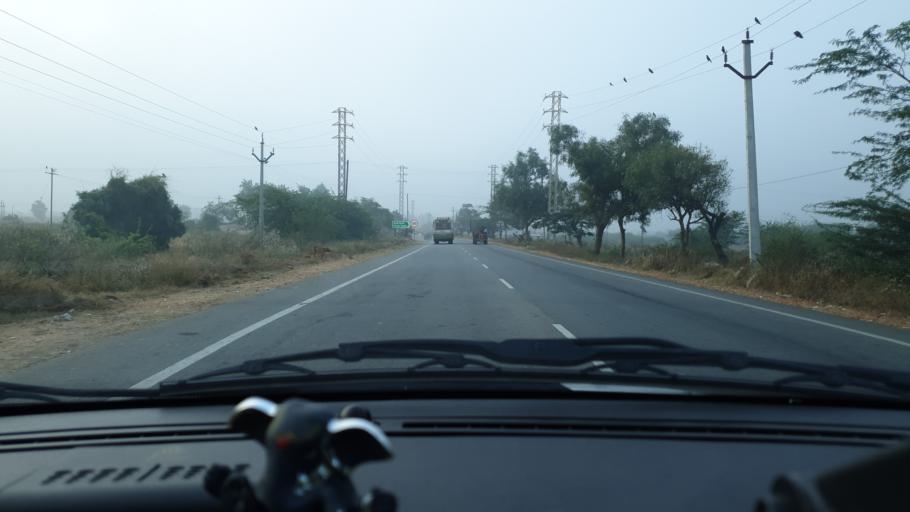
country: IN
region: Telangana
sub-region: Mahbubnagar
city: Farrukhnagar
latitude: 16.8883
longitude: 78.5293
